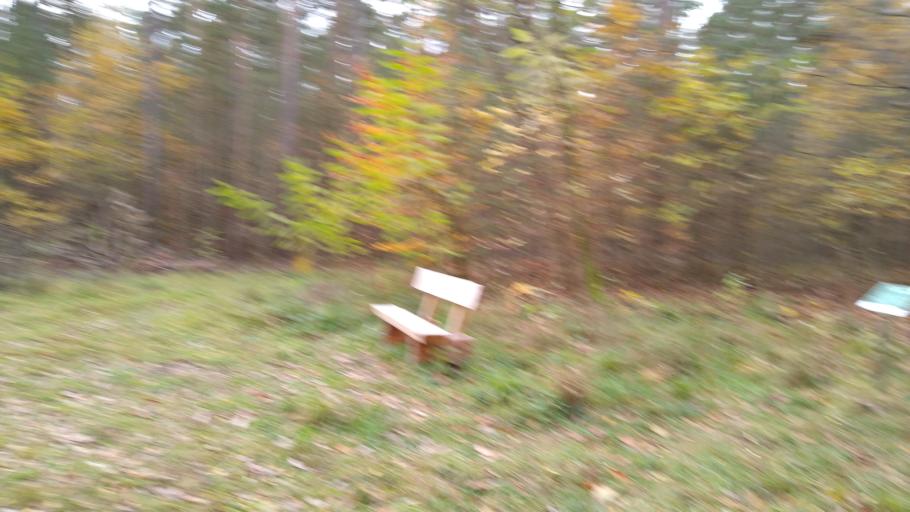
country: DE
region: Bavaria
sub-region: Regierungsbezirk Mittelfranken
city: Kalchreuth
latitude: 49.5411
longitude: 11.1032
